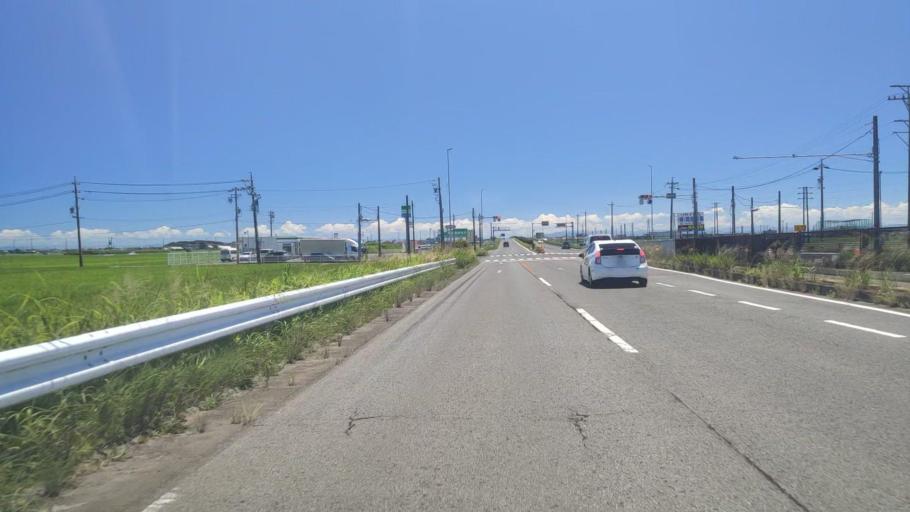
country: JP
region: Mie
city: Suzuka
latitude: 34.8857
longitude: 136.5986
